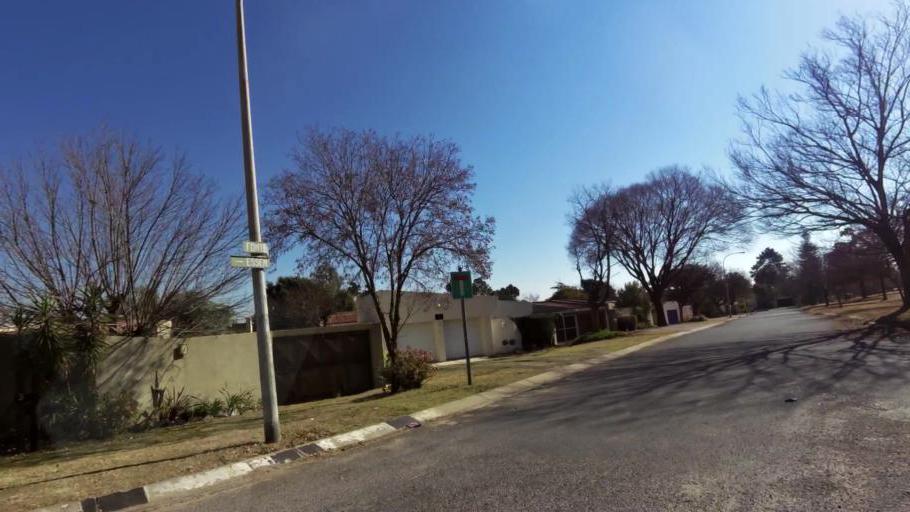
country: ZA
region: Gauteng
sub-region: City of Johannesburg Metropolitan Municipality
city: Johannesburg
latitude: -26.2443
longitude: 27.9935
